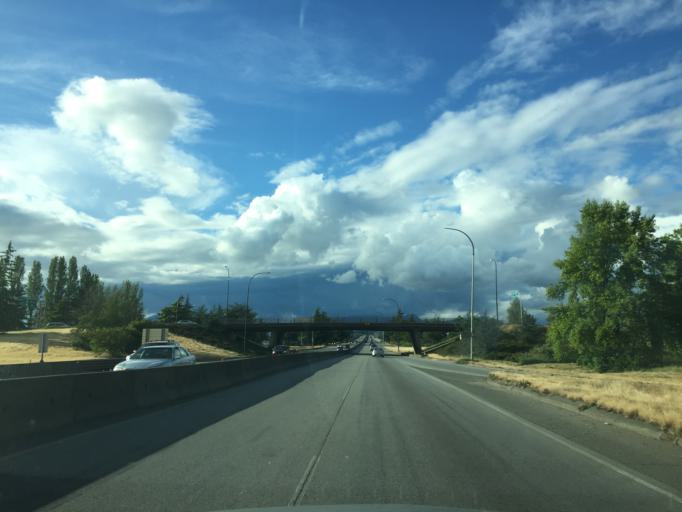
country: CA
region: British Columbia
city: Richmond
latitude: 49.1905
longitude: -123.0774
